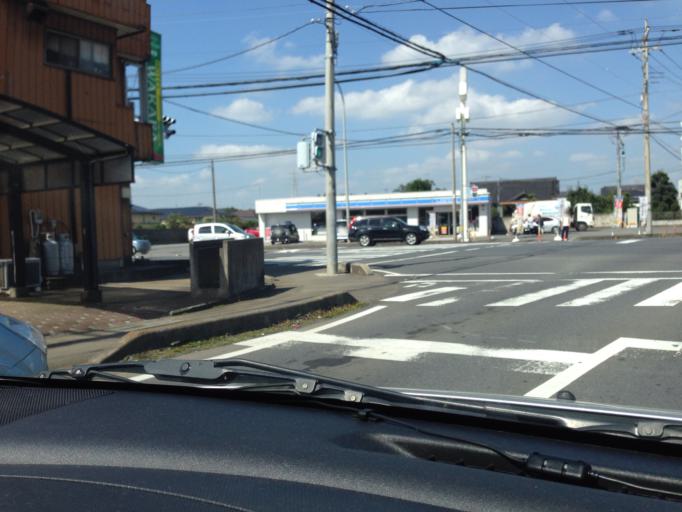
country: JP
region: Ibaraki
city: Naka
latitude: 36.0570
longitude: 140.1513
